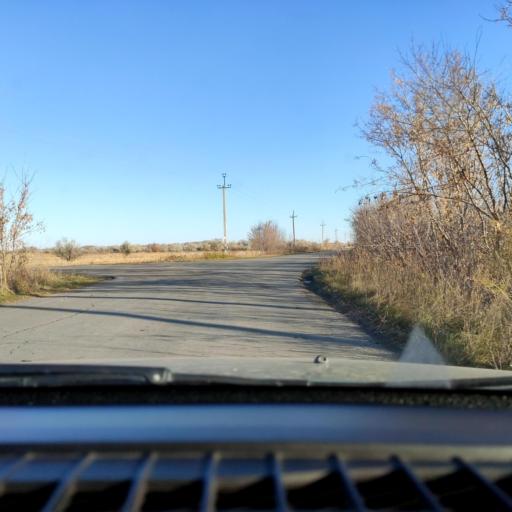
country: RU
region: Samara
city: Tol'yatti
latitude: 53.6487
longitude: 49.3205
